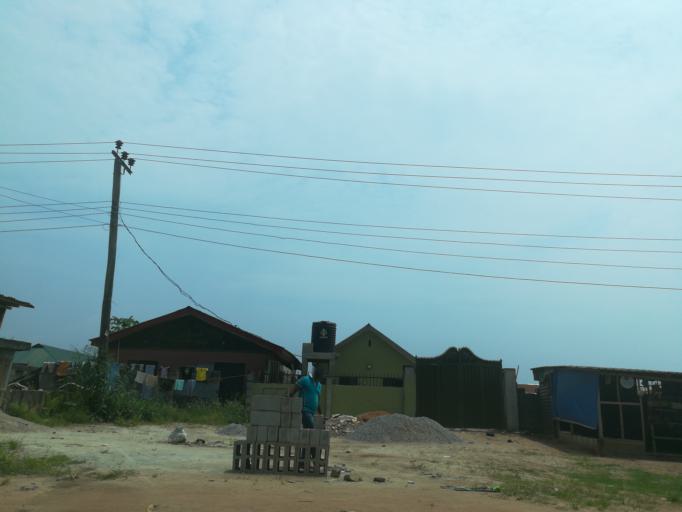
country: NG
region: Lagos
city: Ikorodu
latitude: 6.6039
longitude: 3.6036
